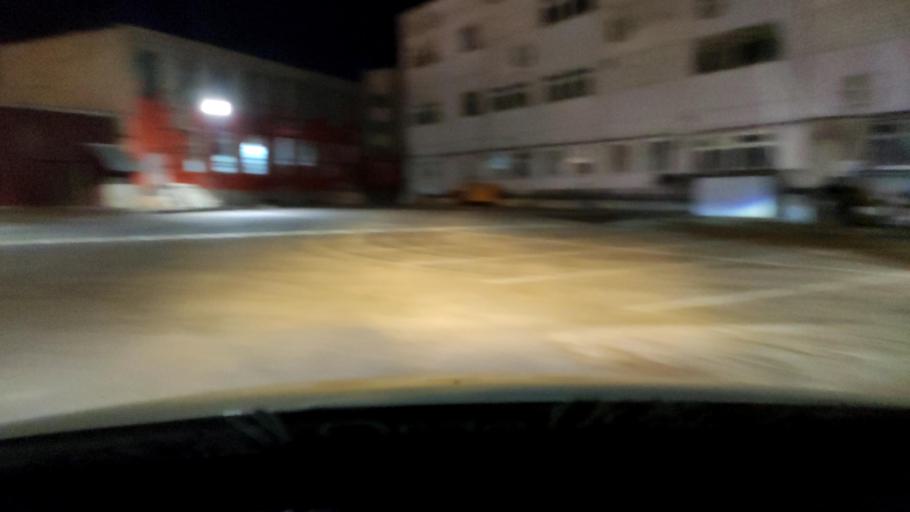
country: RU
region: Voronezj
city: Voronezh
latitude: 51.6768
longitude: 39.2013
